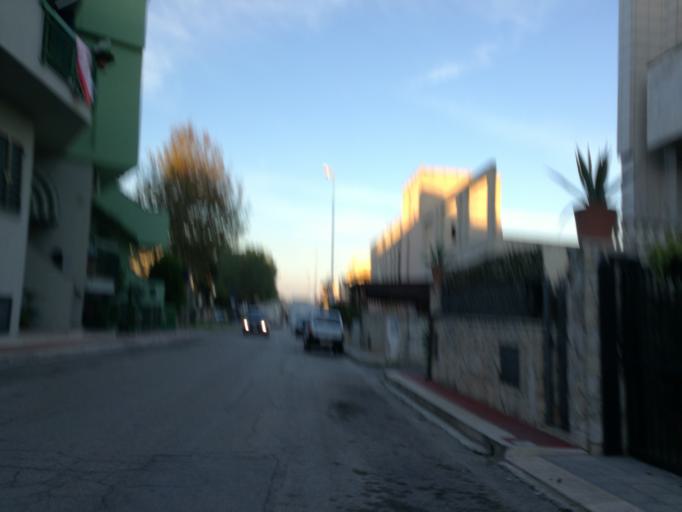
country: IT
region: Apulia
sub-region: Provincia di Bari
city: Adelfia
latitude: 40.9996
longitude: 16.8790
